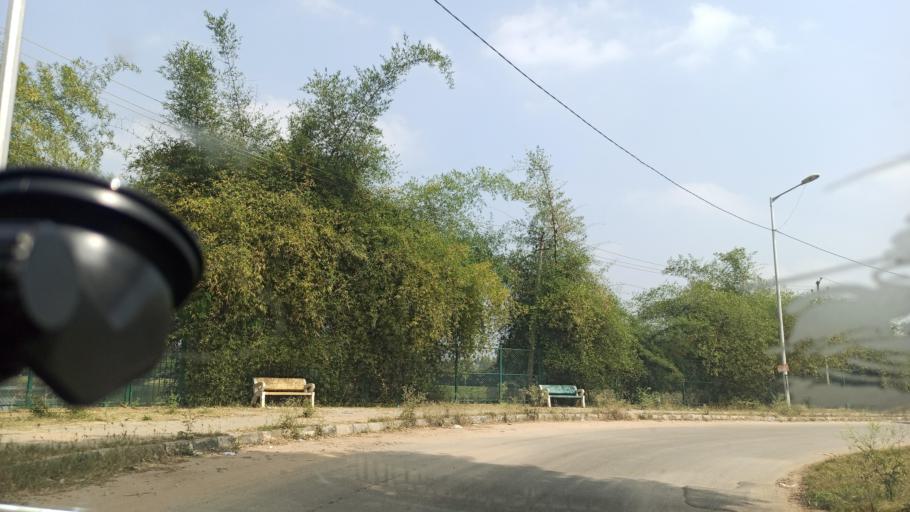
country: IN
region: Karnataka
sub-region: Bangalore Urban
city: Yelahanka
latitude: 13.0819
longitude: 77.6119
